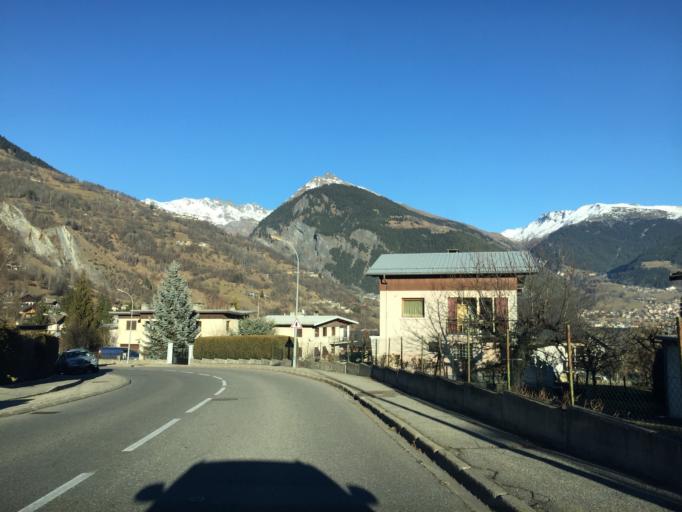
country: FR
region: Rhone-Alpes
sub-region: Departement de la Savoie
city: Bourg-Saint-Maurice
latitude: 45.6143
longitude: 6.7621
